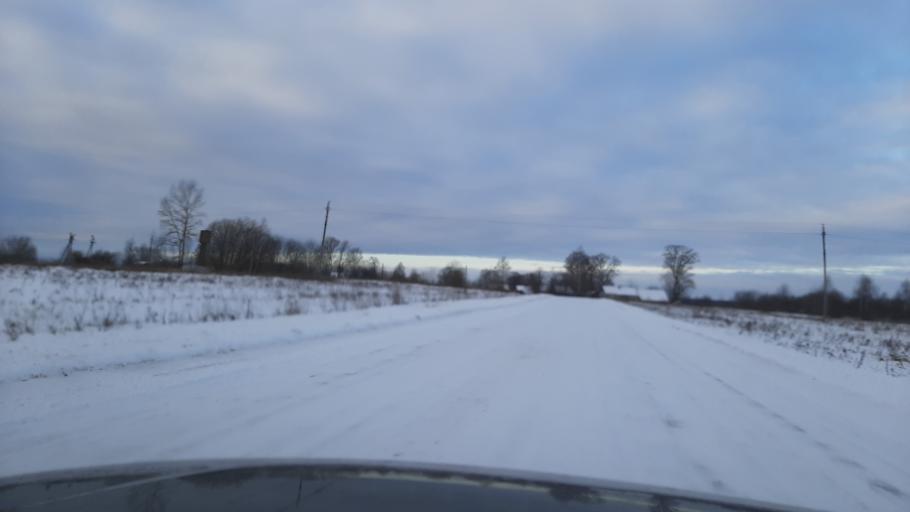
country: RU
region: Kostroma
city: Kosmynino
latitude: 57.4842
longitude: 40.8162
